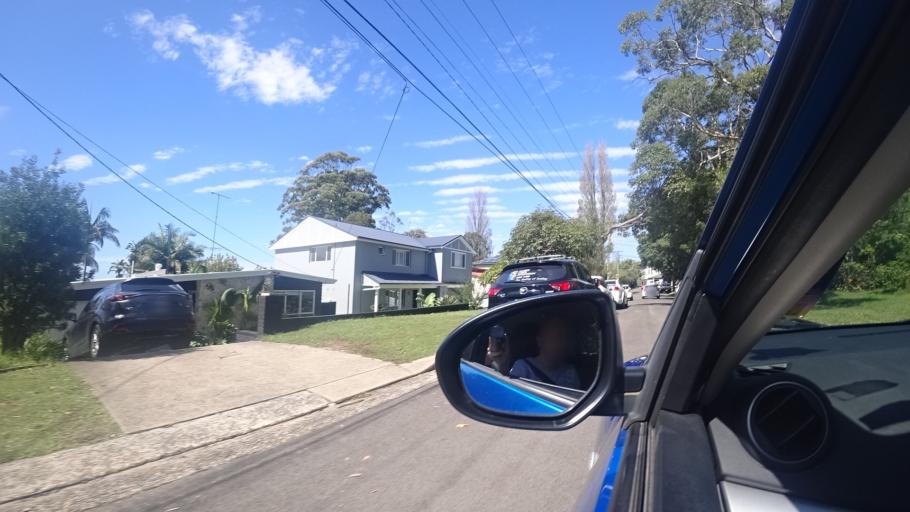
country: AU
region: New South Wales
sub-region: Warringah
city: Allambie Heights
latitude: -33.7613
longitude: 151.2488
